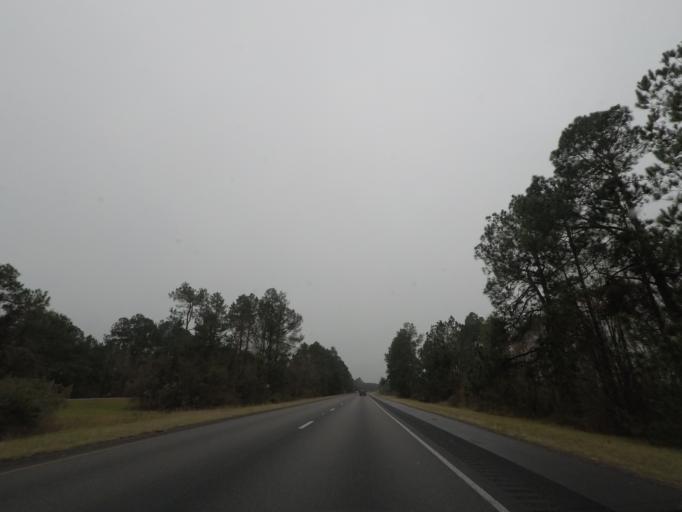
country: US
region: South Carolina
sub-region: Sumter County
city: East Sumter
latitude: 33.8793
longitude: -80.1018
